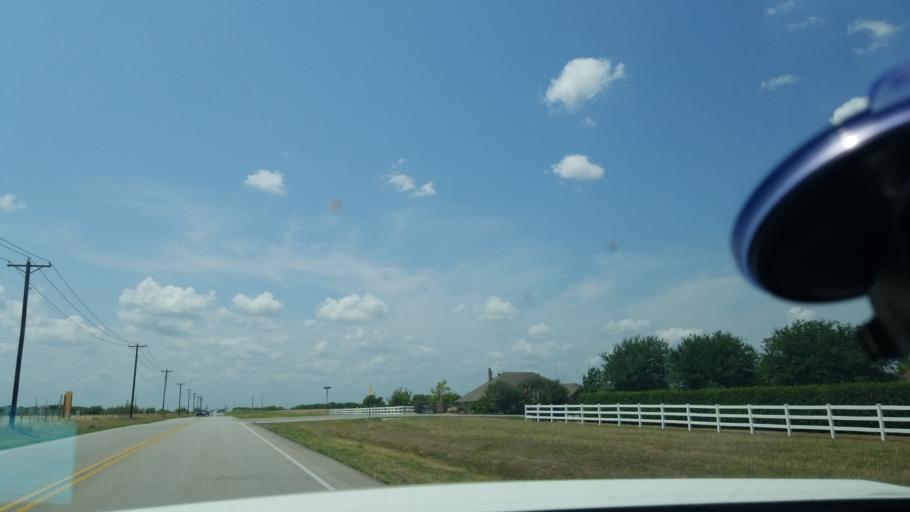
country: US
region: Texas
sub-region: Tarrant County
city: Eagle Mountain
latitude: 32.9245
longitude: -97.4008
